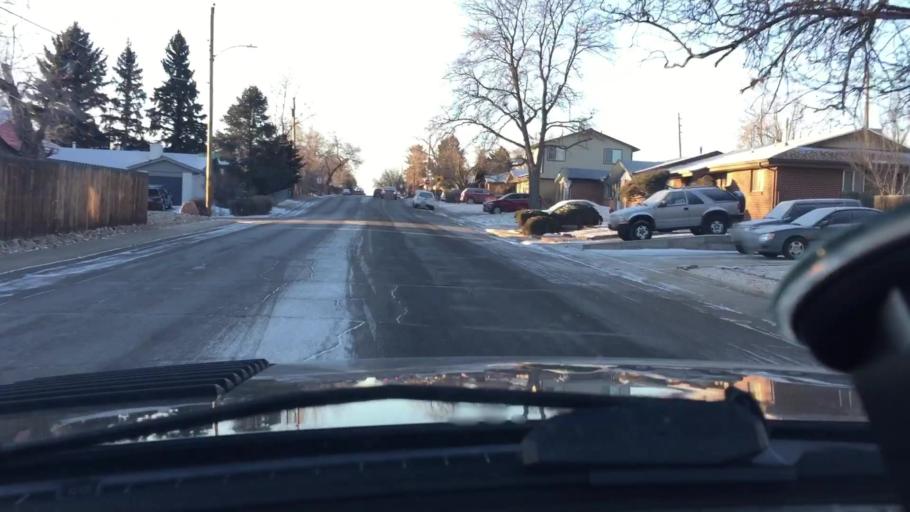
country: US
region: Colorado
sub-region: Adams County
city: Northglenn
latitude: 39.8842
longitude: -105.0056
